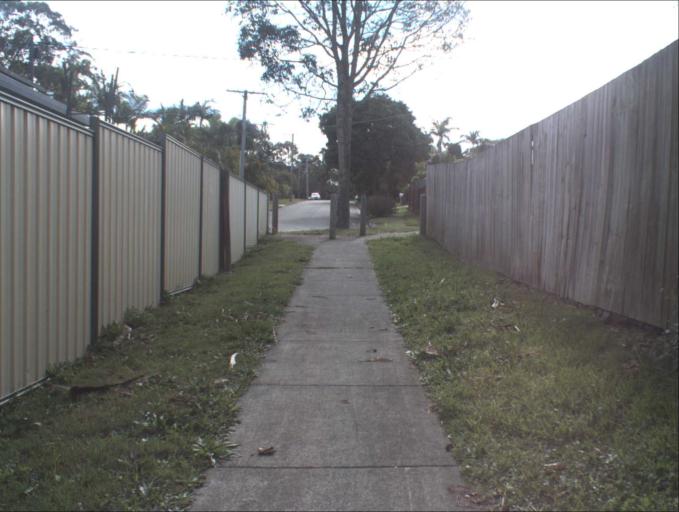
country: AU
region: Queensland
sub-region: Logan
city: Park Ridge South
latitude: -27.6860
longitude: 153.0344
